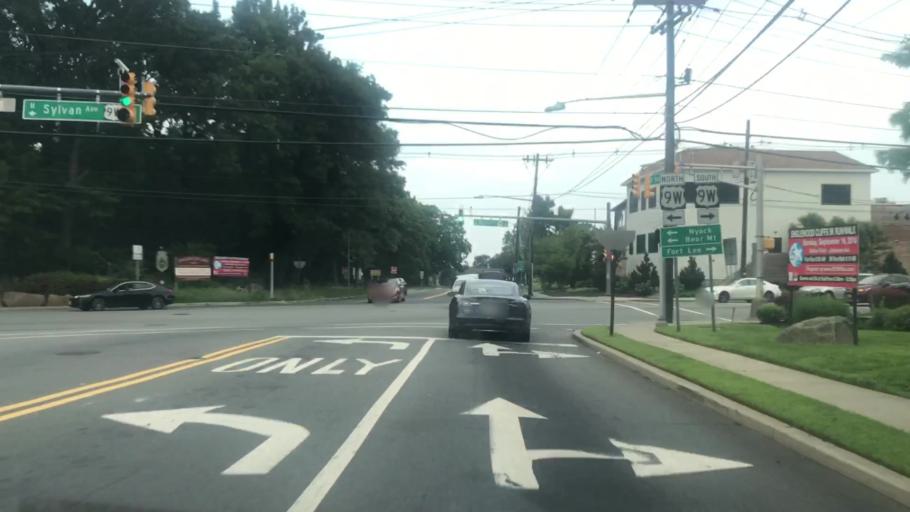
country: US
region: New Jersey
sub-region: Bergen County
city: Englewood Cliffs
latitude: 40.8807
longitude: -73.9516
